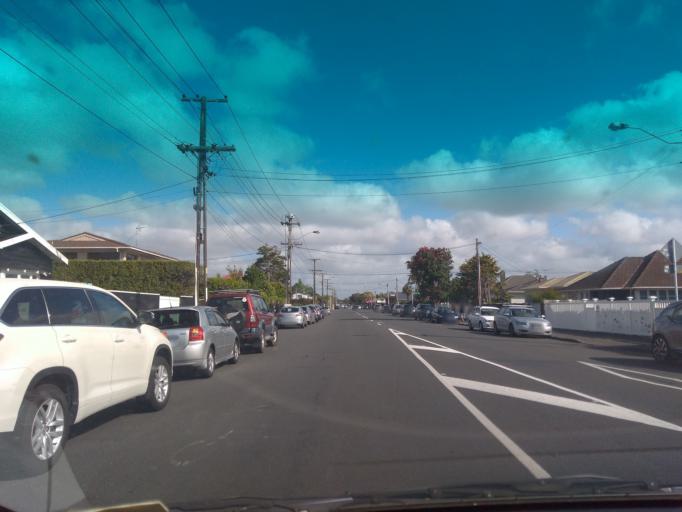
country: NZ
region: Auckland
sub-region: Auckland
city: Rosebank
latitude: -36.8613
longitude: 174.7034
